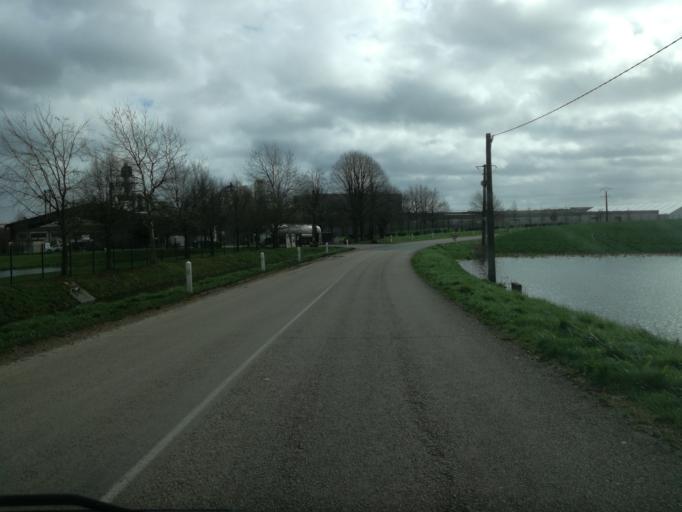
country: FR
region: Haute-Normandie
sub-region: Departement de la Seine-Maritime
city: Valliquerville
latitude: 49.6109
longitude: 0.6643
